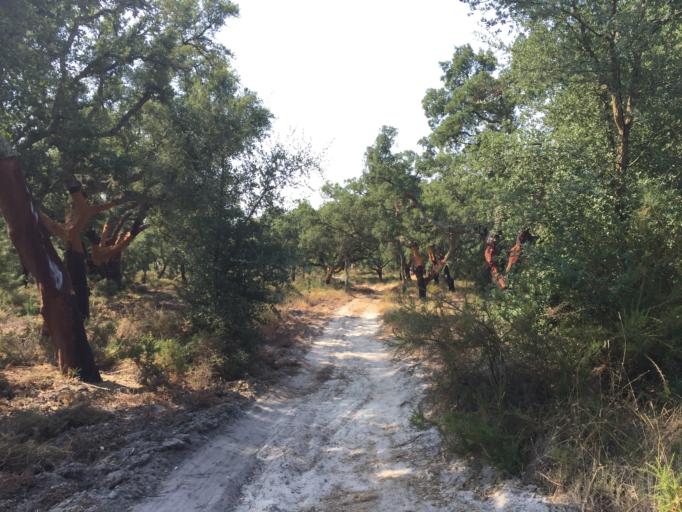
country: PT
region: Setubal
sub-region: Setubal
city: Setubal
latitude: 38.5882
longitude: -8.6878
